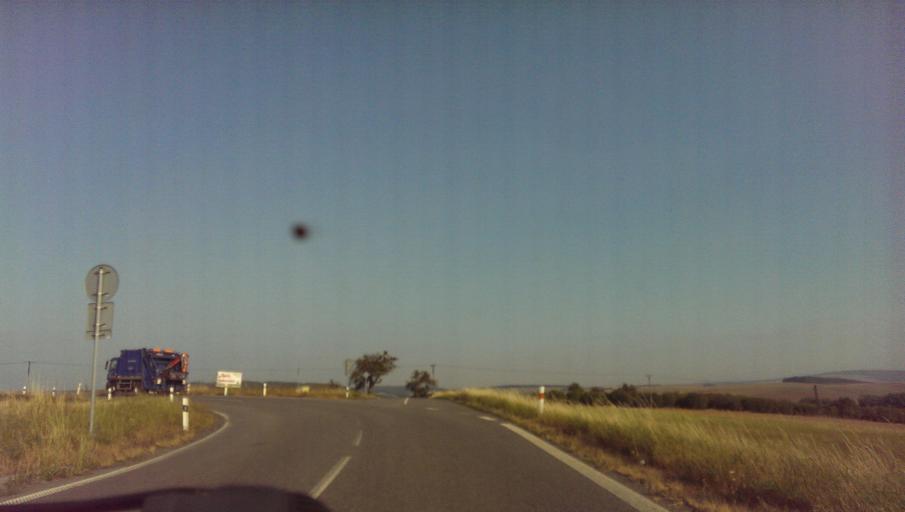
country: CZ
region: Zlin
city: Korycany
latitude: 49.1075
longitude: 17.1533
